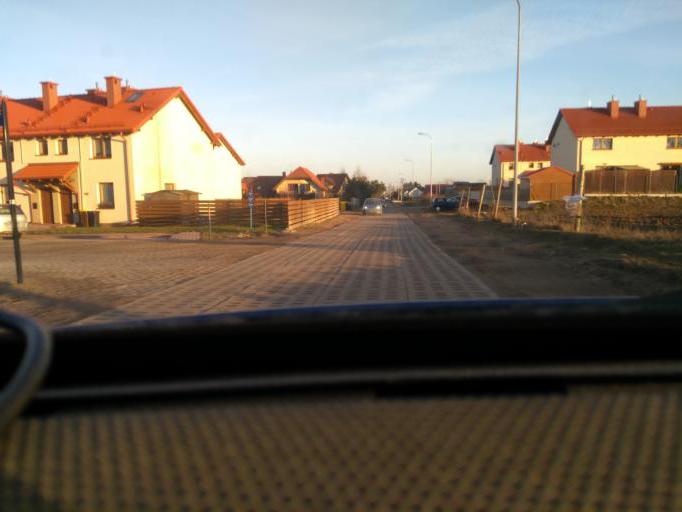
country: PL
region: Pomeranian Voivodeship
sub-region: Powiat kartuski
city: Banino
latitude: 54.3858
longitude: 18.3866
